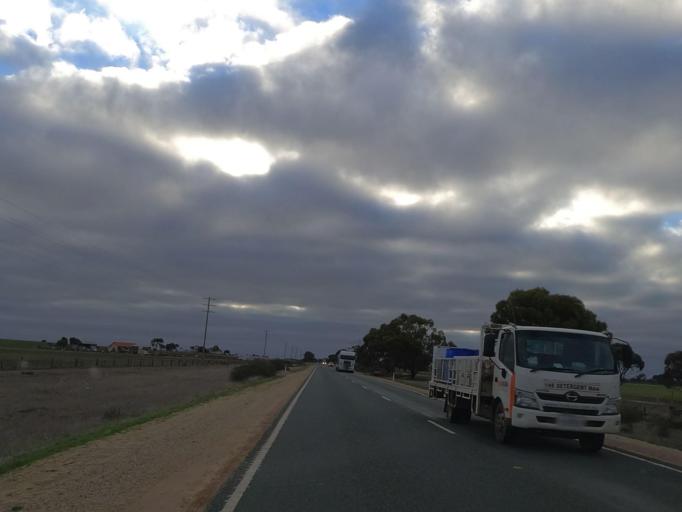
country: AU
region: Victoria
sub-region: Swan Hill
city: Swan Hill
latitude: -35.6449
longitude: 143.8334
